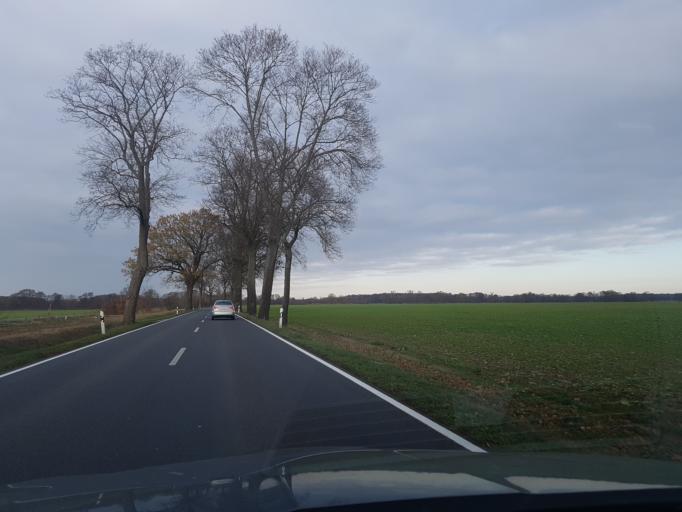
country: DE
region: Brandenburg
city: Golssen
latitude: 51.9555
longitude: 13.6336
